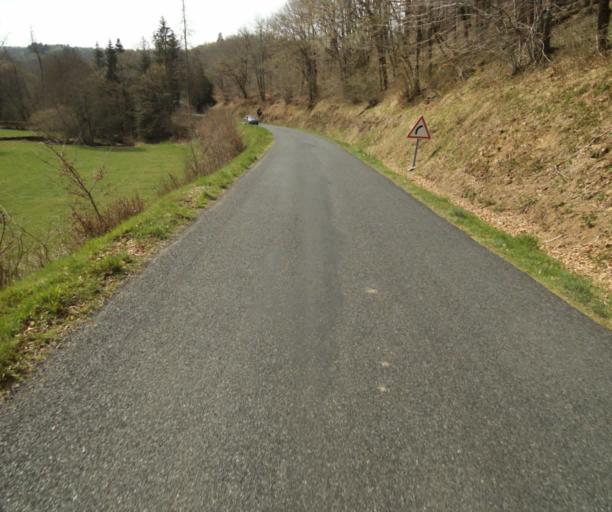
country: FR
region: Limousin
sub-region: Departement de la Correze
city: Naves
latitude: 45.3386
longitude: 1.7944
